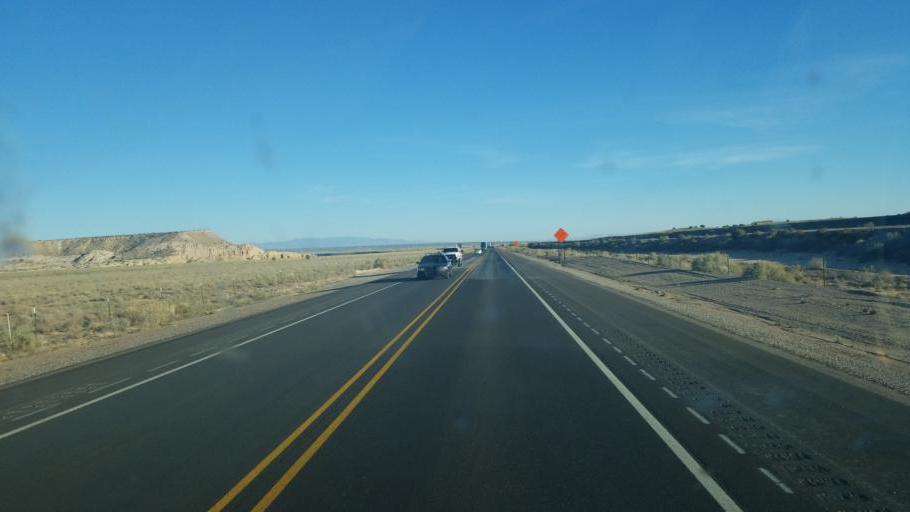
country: US
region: New Mexico
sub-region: Cibola County
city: Laguna
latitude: 34.9098
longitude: -107.0972
